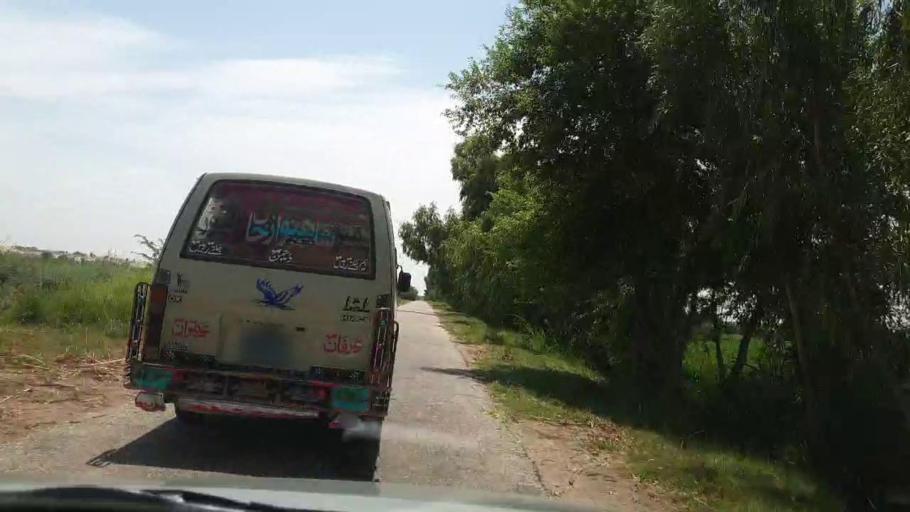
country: PK
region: Sindh
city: Bozdar
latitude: 27.0696
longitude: 68.9788
